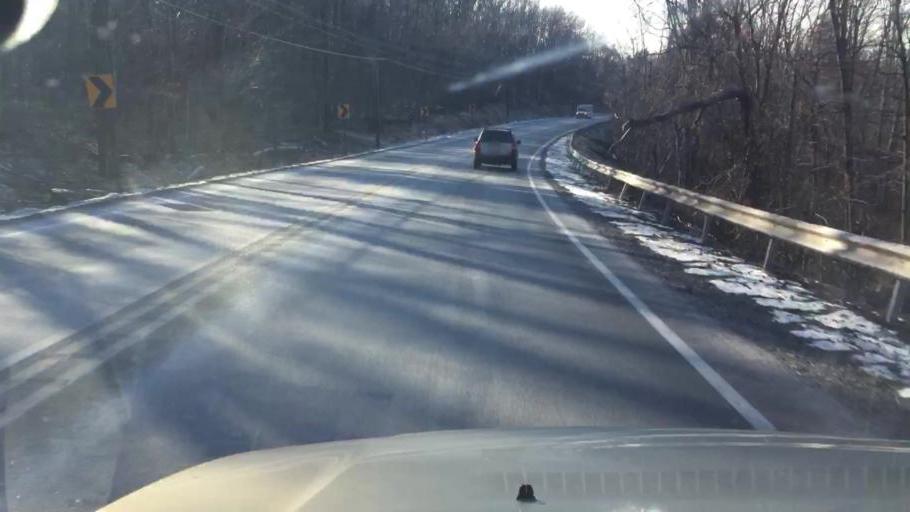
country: US
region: Pennsylvania
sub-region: Luzerne County
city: Conyngham
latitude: 41.0336
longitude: -76.1152
